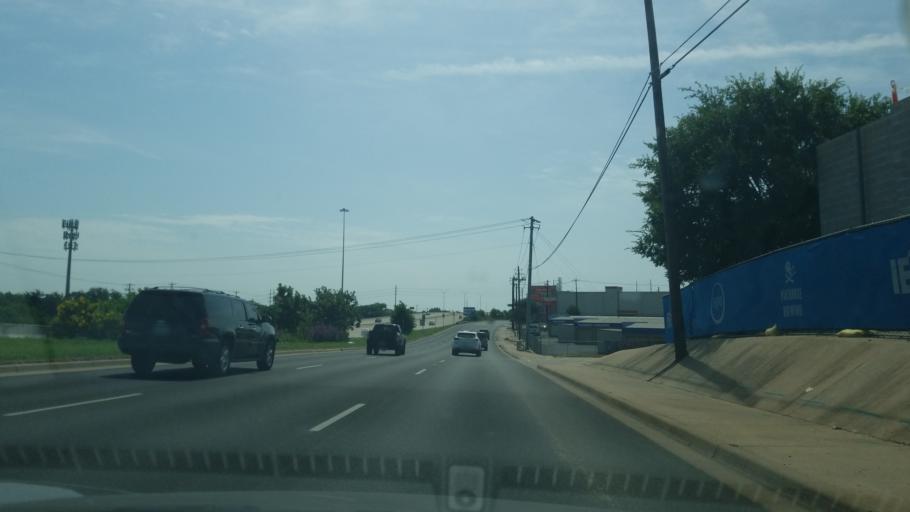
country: US
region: Texas
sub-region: Travis County
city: Austin
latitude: 30.2156
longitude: -97.7422
